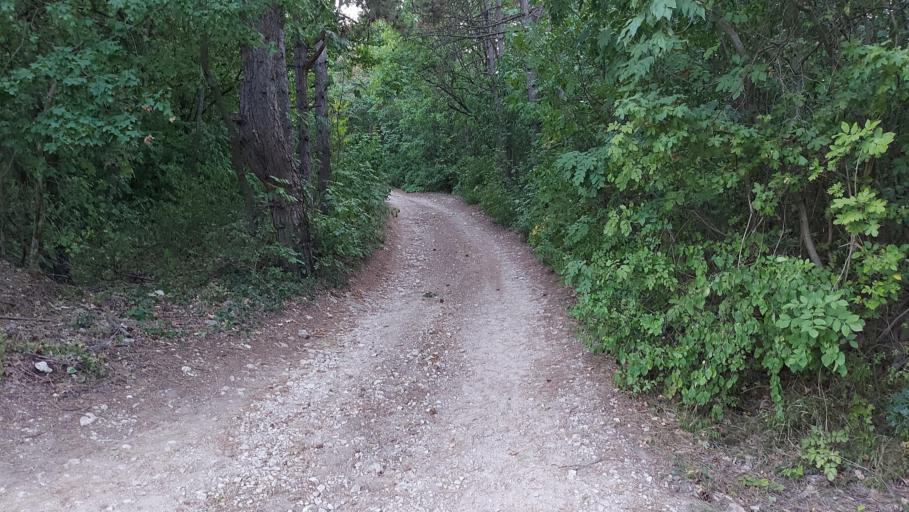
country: HU
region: Veszprem
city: Szentkiralyszabadja
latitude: 47.0458
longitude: 17.9897
